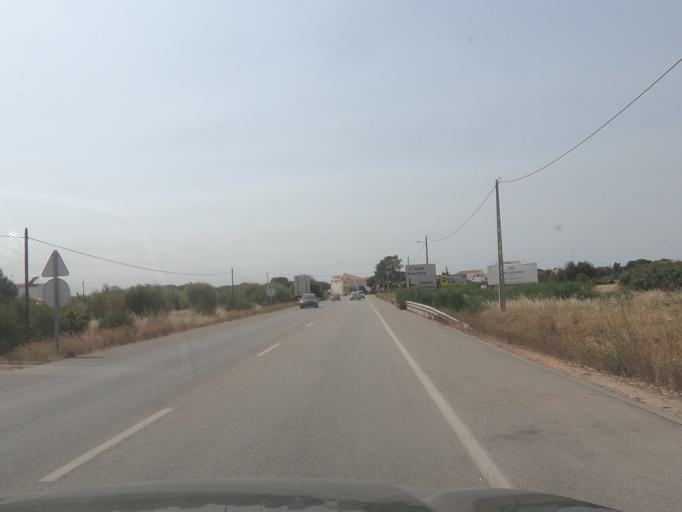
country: PT
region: Faro
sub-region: Loule
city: Almancil
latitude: 37.0943
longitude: -8.0622
